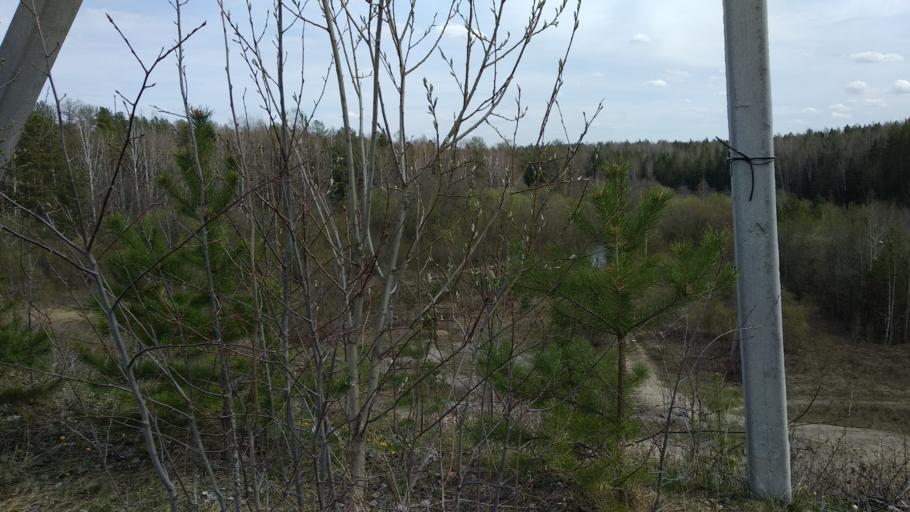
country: RU
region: Sverdlovsk
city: Rudnichnyy
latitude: 59.5981
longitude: 60.3838
